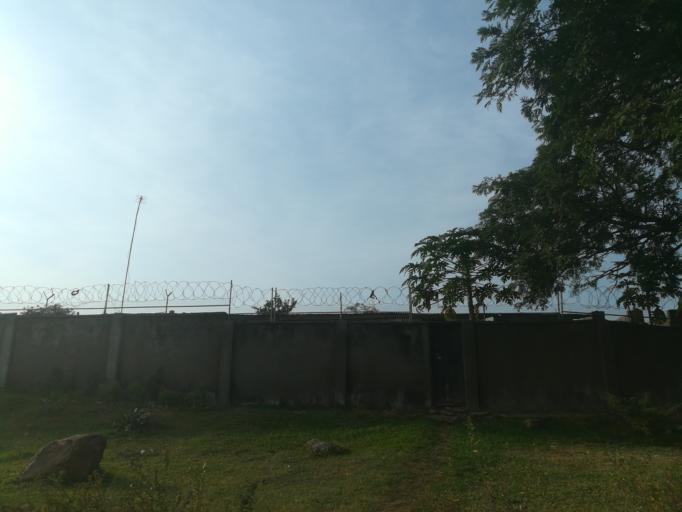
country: NG
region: Abuja Federal Capital Territory
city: Abuja
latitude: 9.0936
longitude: 7.3735
